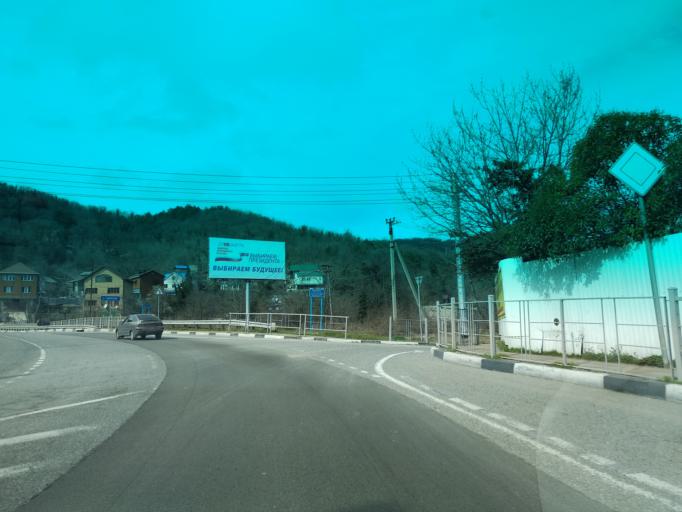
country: RU
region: Krasnodarskiy
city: Shepsi
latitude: 44.0419
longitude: 39.1508
